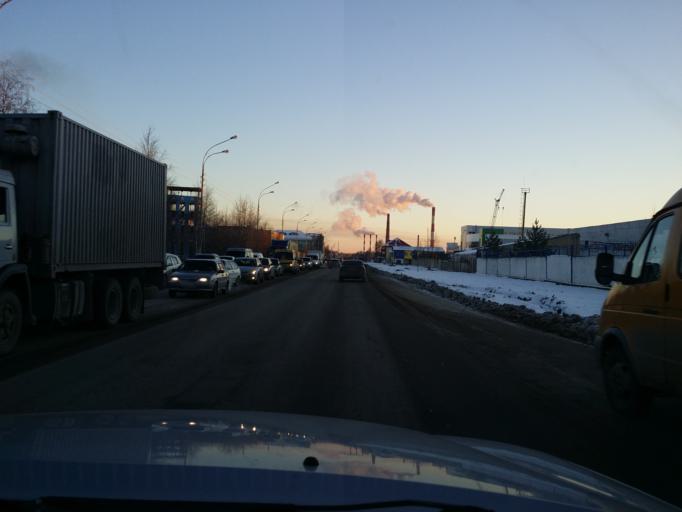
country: RU
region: Khanty-Mansiyskiy Avtonomnyy Okrug
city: Nizhnevartovsk
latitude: 60.9445
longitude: 76.5482
